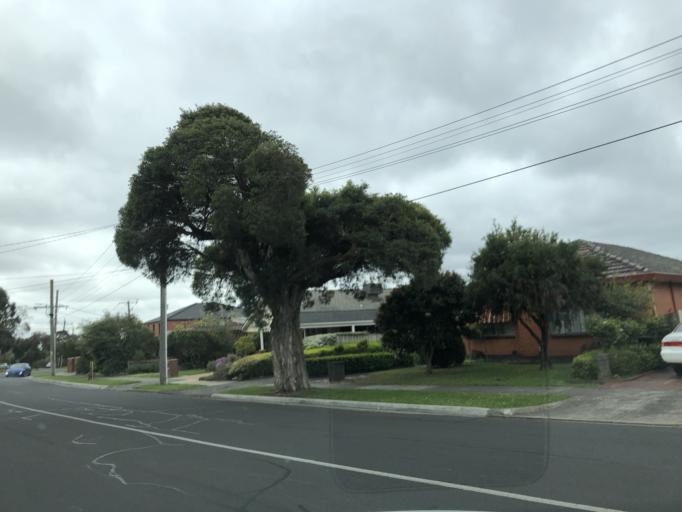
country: AU
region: Victoria
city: Burwood East
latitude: -37.8558
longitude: 145.1477
